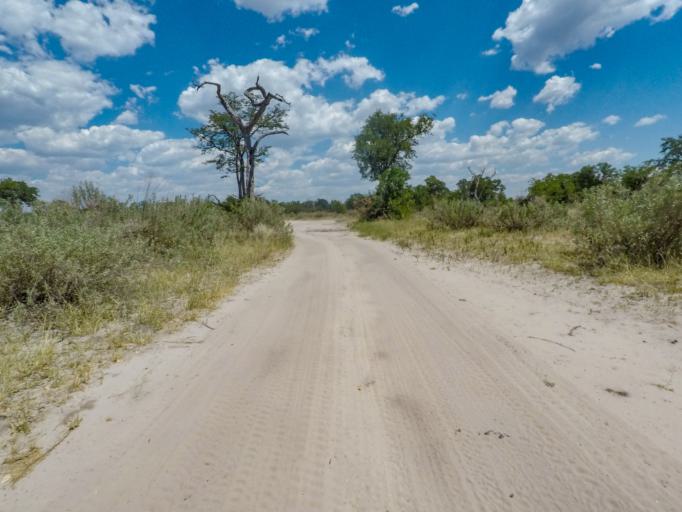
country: BW
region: North West
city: Maun
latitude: -19.1764
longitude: 23.7501
